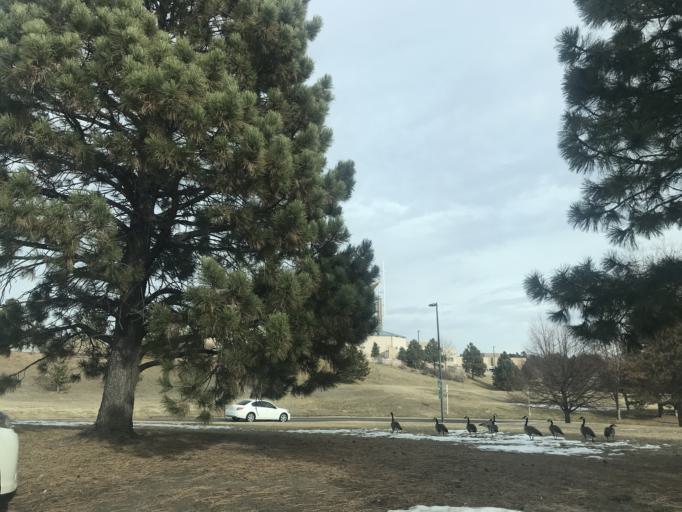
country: US
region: Colorado
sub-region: Douglas County
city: Highlands Ranch
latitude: 39.5658
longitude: -104.9969
